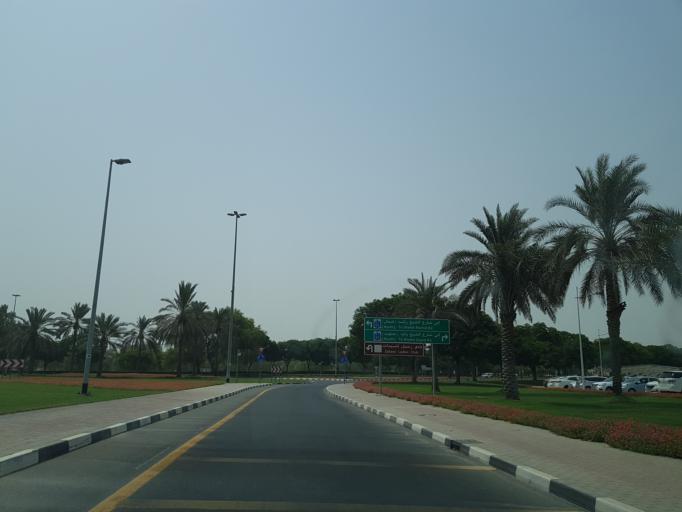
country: AE
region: Ash Shariqah
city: Sharjah
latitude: 25.2287
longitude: 55.2994
